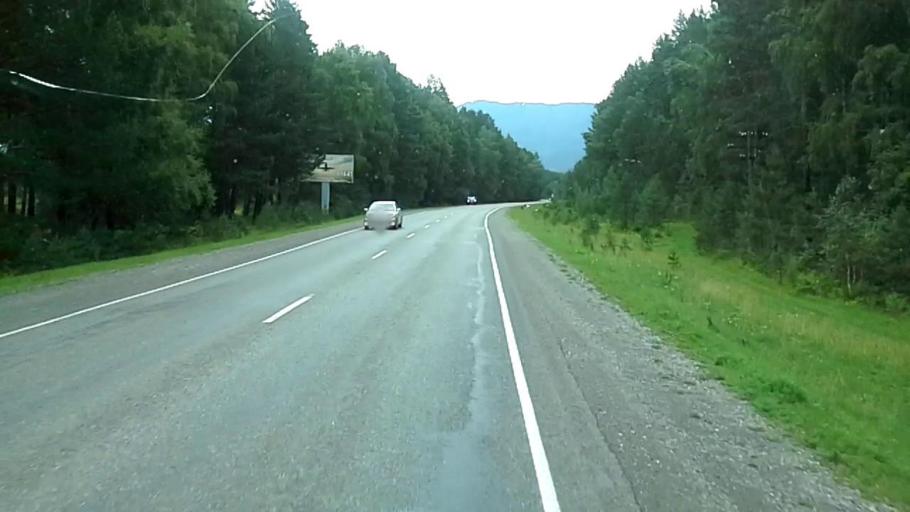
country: RU
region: Altay
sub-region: Mayminskiy Rayon
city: Manzherok
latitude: 51.8336
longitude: 85.7476
